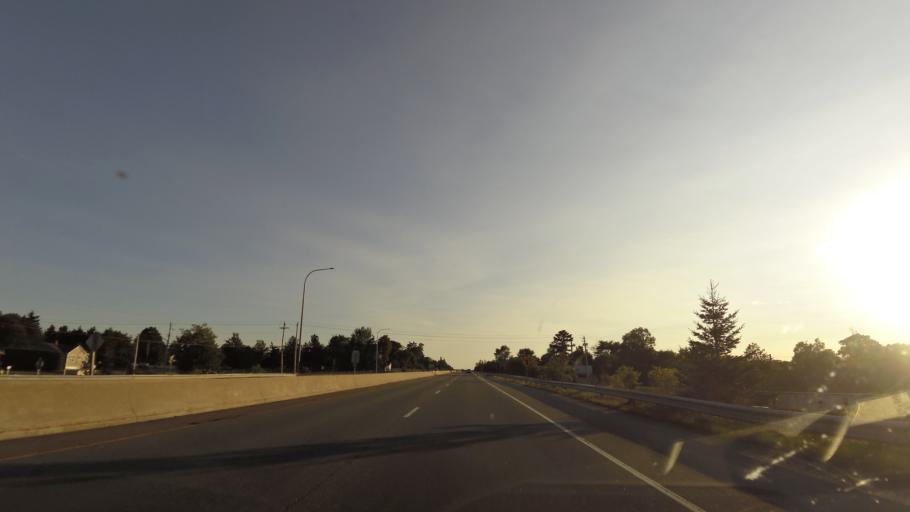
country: CA
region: New Brunswick
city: Salisbury
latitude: 45.9309
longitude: -65.1667
